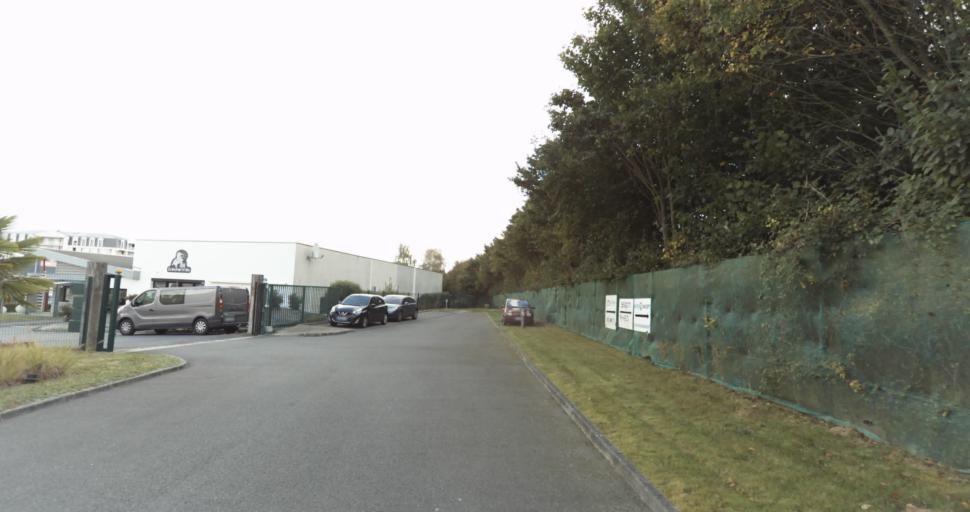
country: FR
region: Brittany
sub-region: Departement d'Ille-et-Vilaine
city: Cesson-Sevigne
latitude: 48.1074
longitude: -1.6129
